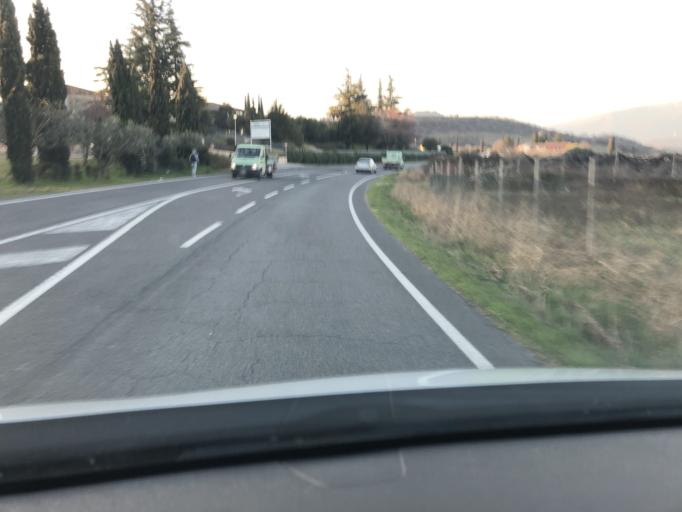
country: IT
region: Veneto
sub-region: Provincia di Verona
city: Pastrengo
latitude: 45.4812
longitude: 10.8162
